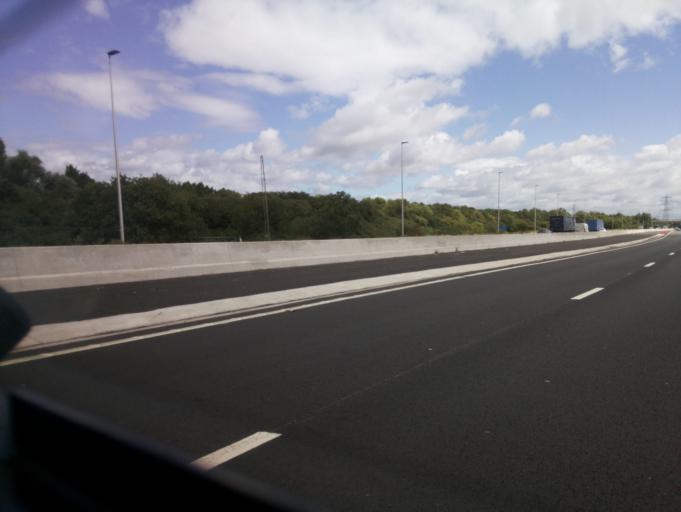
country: GB
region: Wales
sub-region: Monmouthshire
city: Rogiet
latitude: 51.5817
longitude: -2.7884
